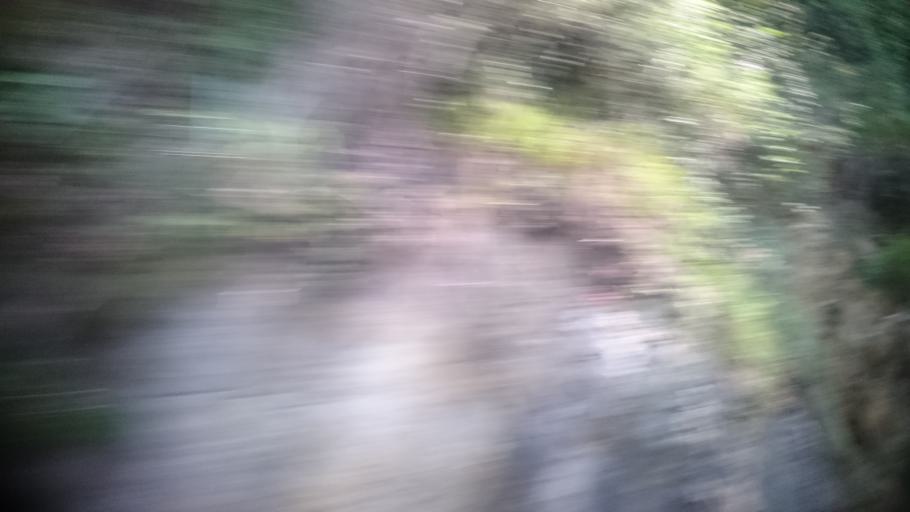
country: ES
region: Asturias
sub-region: Province of Asturias
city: Amieva
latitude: 43.3032
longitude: -5.0411
